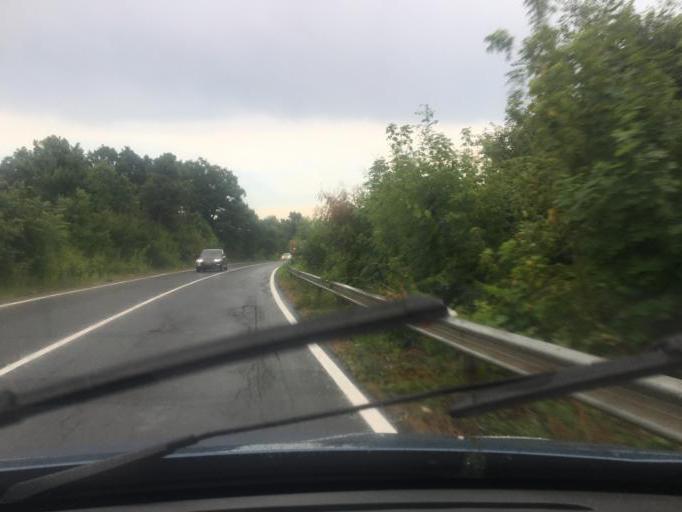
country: BG
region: Burgas
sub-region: Obshtina Pomorie
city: Pomorie
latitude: 42.5653
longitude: 27.5914
